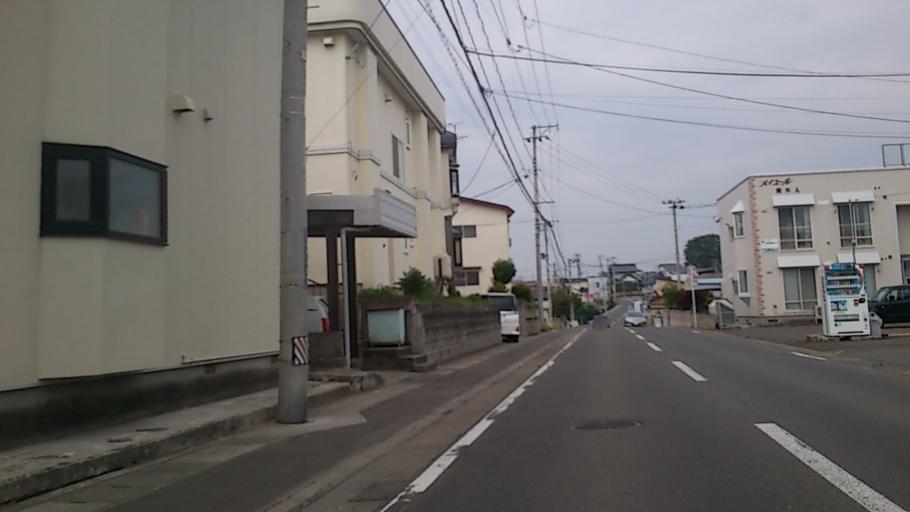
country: JP
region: Aomori
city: Hirosaki
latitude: 40.5943
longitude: 140.4558
